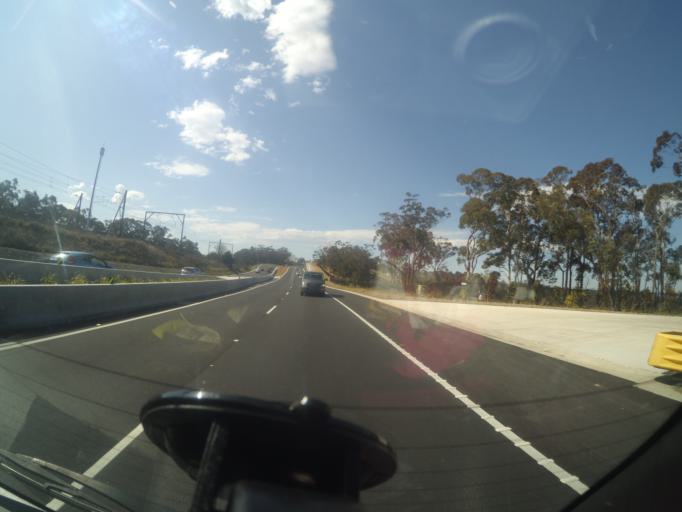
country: AU
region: New South Wales
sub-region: Blue Mountains Municipality
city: Lawson
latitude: -33.7257
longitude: 150.4021
